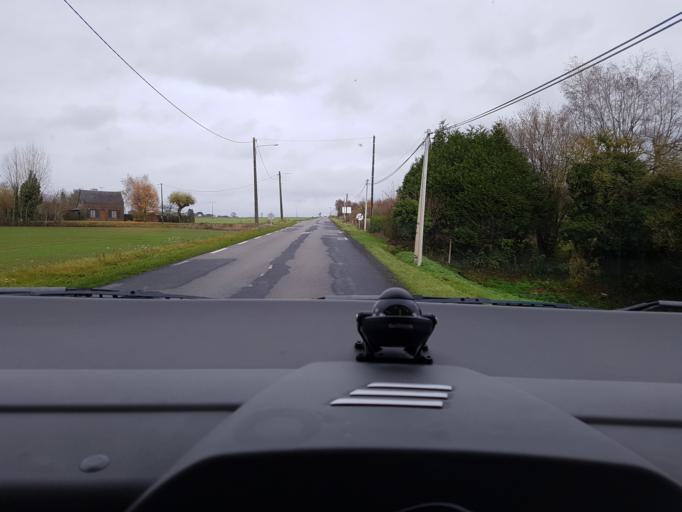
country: FR
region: Haute-Normandie
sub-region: Departement de la Seine-Maritime
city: Gournay-en-Bray
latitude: 49.4888
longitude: 1.7530
